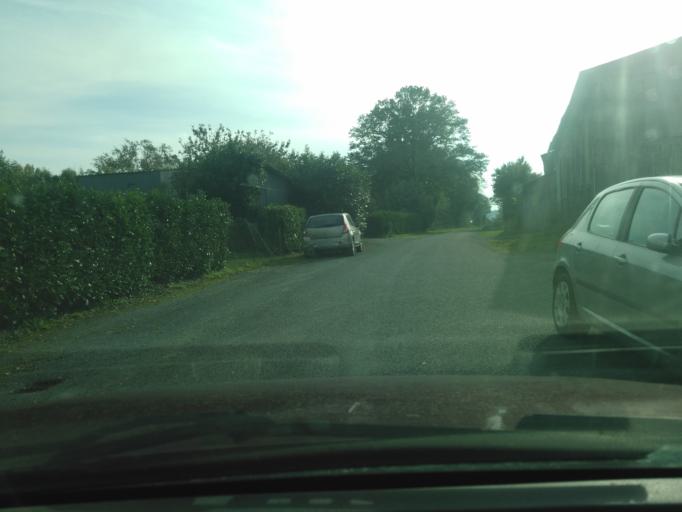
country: FR
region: Pays de la Loire
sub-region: Departement de la Vendee
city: Les Essarts
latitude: 46.7533
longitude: -1.2506
